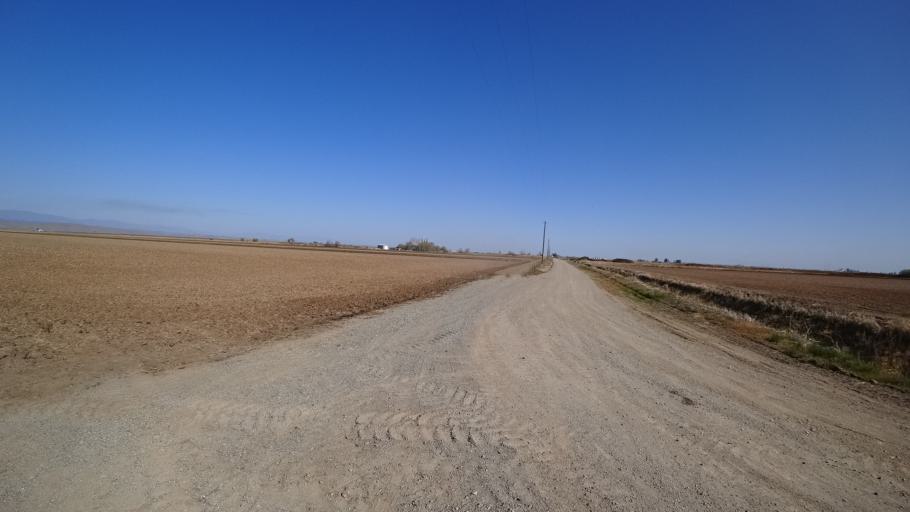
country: US
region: California
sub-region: Glenn County
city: Willows
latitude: 39.4290
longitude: -122.2302
